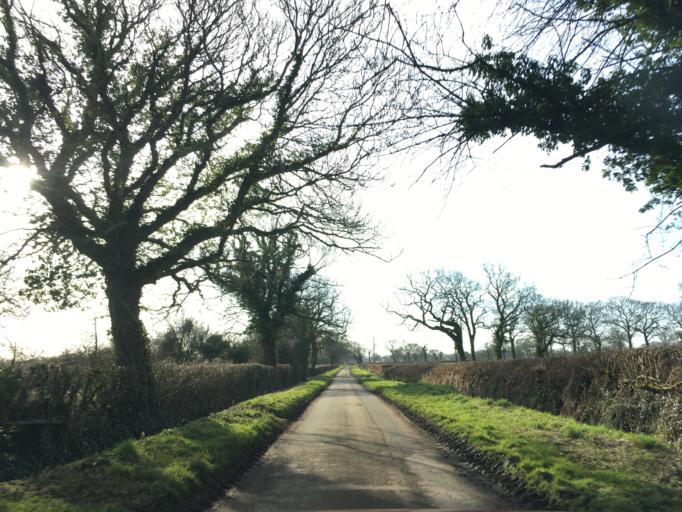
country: GB
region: England
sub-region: South Gloucestershire
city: Yate
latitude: 51.5562
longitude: -2.4453
